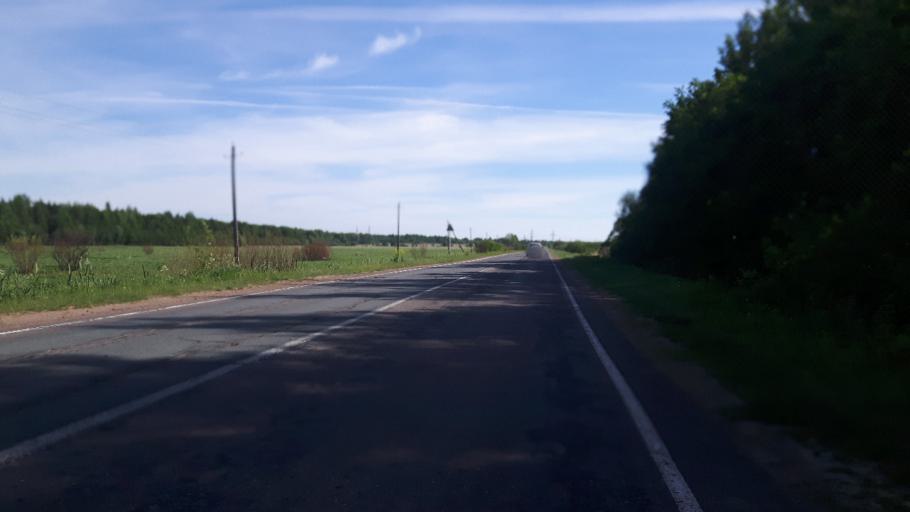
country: RU
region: Leningrad
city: Ivangorod
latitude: 59.4112
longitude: 28.3844
